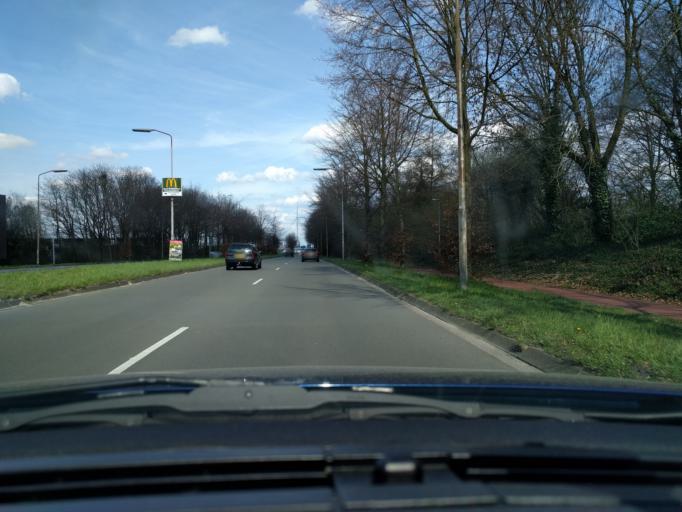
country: NL
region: North Brabant
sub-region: Gemeente Eindhoven
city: Meerhoven
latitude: 51.4287
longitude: 5.4131
